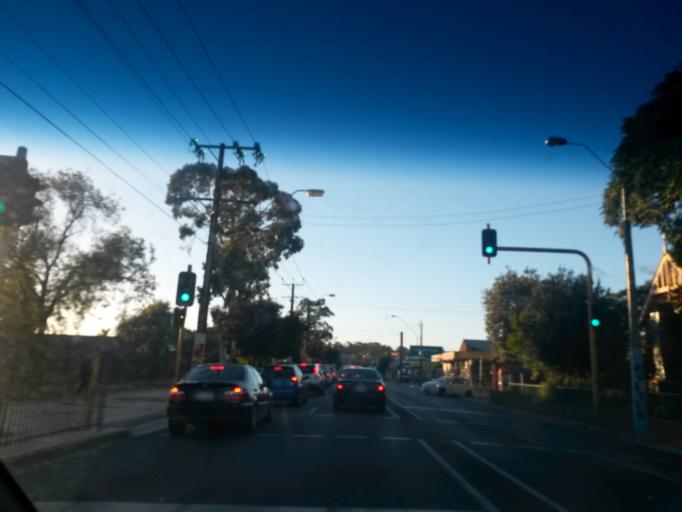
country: AU
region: South Australia
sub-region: Adelaide
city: North Adelaide
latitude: -34.8946
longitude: 138.5803
